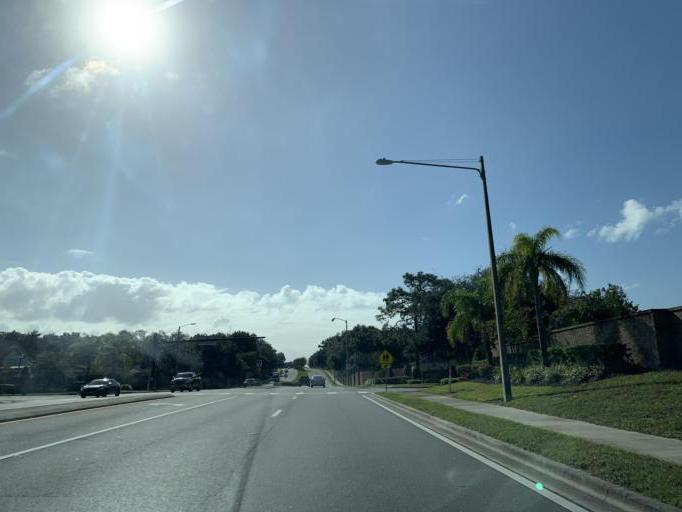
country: US
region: Florida
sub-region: Orange County
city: Clarcona
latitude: 28.6312
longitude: -81.4765
